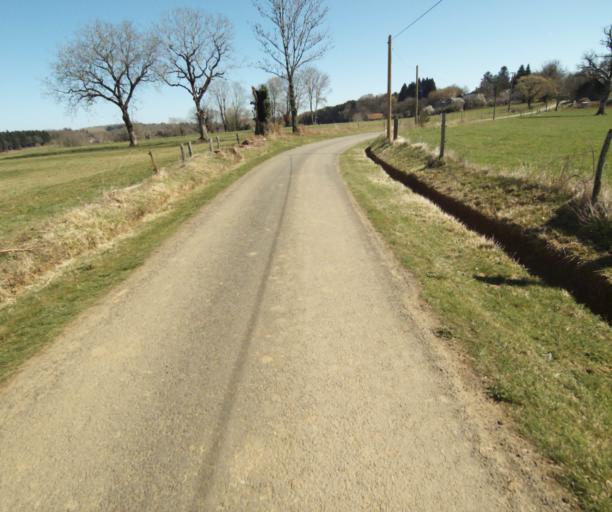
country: FR
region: Limousin
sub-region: Departement de la Correze
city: Seilhac
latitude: 45.3841
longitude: 1.6852
